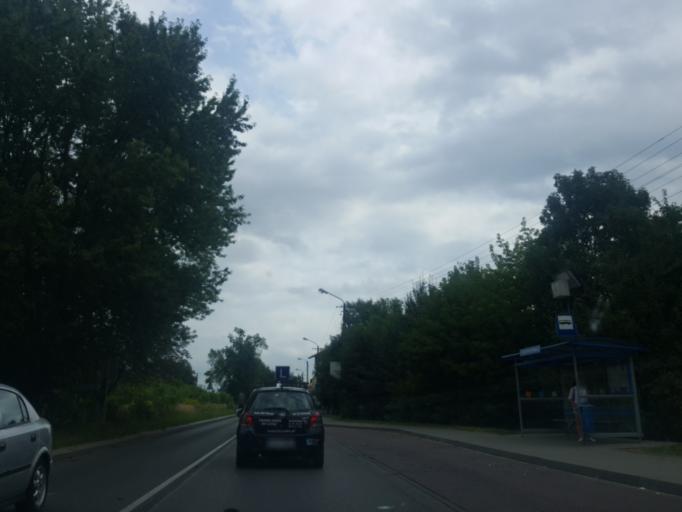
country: PL
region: Lesser Poland Voivodeship
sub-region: Powiat chrzanowski
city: Chrzanow
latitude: 50.1387
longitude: 19.4070
